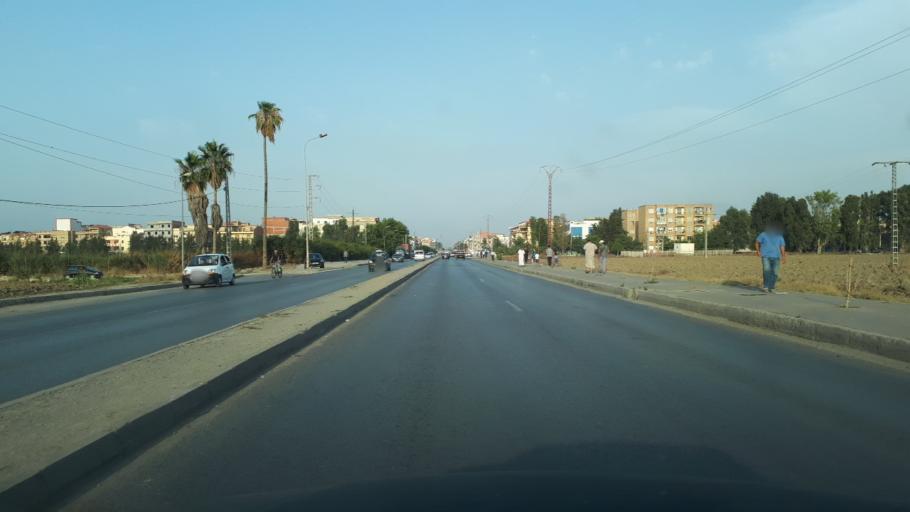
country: DZ
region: Alger
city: Dar el Beida
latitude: 36.7294
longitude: 3.2273
